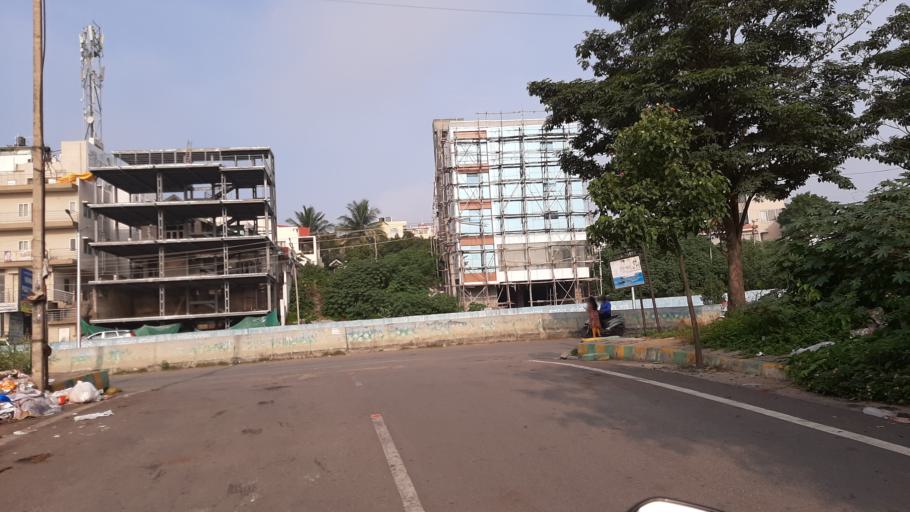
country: IN
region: Karnataka
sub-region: Bangalore Urban
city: Bangalore
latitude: 12.9694
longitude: 77.5126
